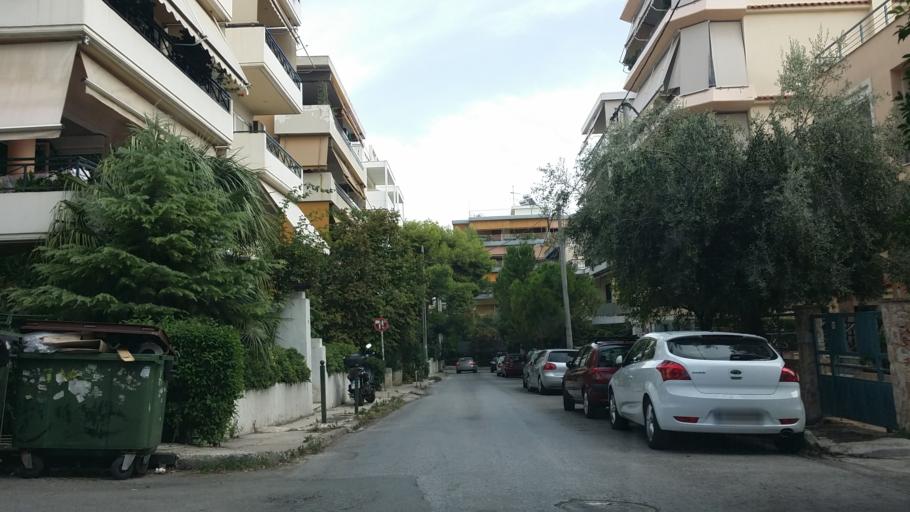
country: GR
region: Attica
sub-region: Nomarchia Athinas
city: Irakleio
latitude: 38.0466
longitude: 23.7731
